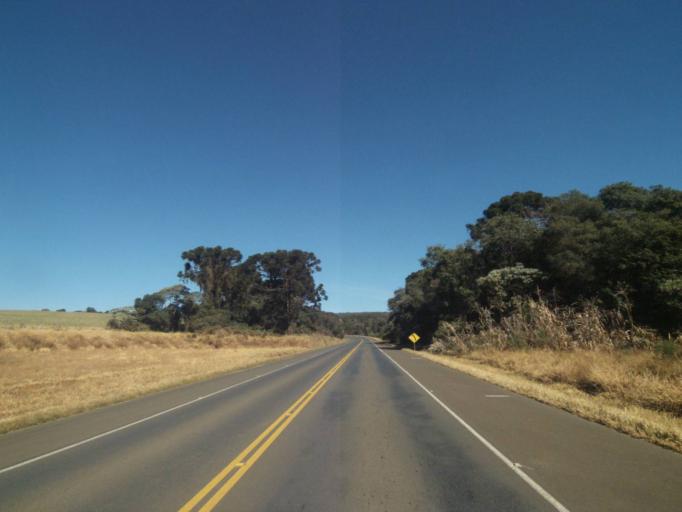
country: BR
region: Parana
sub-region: Tibagi
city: Tibagi
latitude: -24.5503
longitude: -50.4543
